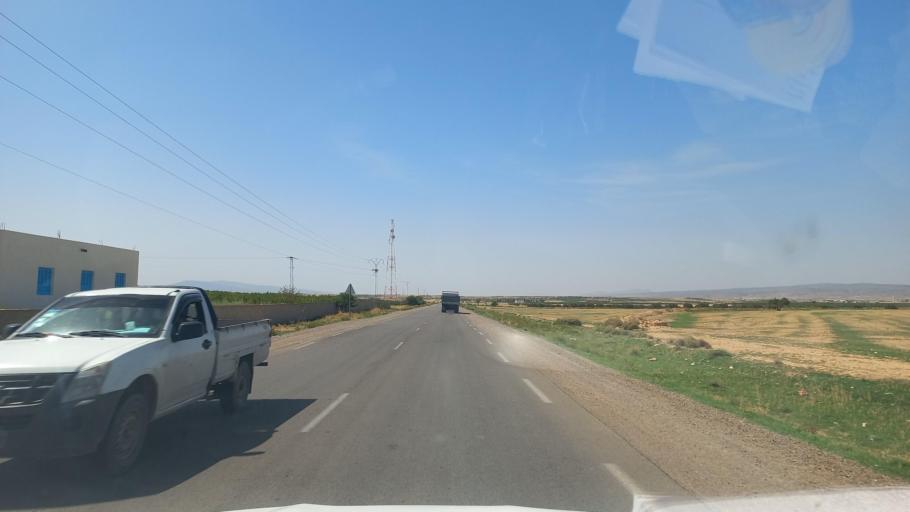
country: TN
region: Al Qasrayn
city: Sbiba
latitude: 35.3779
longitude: 9.1055
